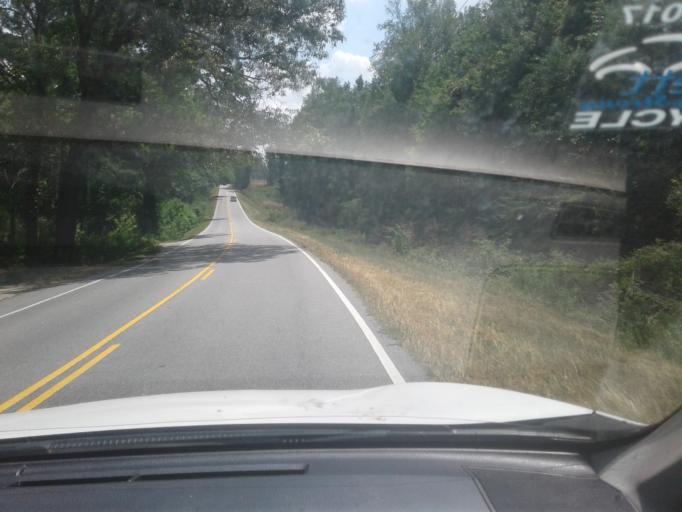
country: US
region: North Carolina
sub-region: Johnston County
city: Benson
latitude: 35.4161
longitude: -78.5400
